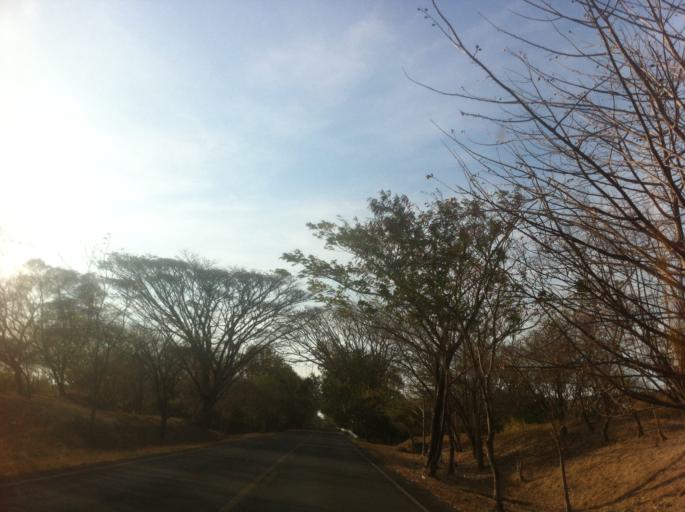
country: NI
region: Rivas
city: Cardenas
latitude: 11.2620
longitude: -85.6433
